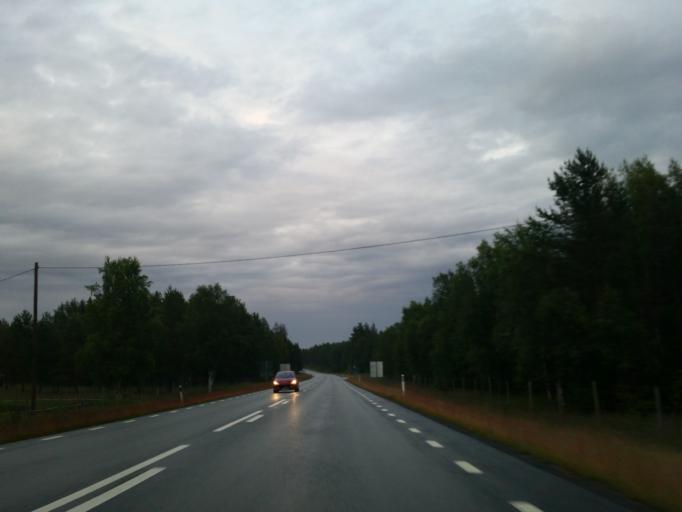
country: SE
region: Vaesterbotten
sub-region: Robertsfors Kommun
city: Robertsfors
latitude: 63.9947
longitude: 20.7722
